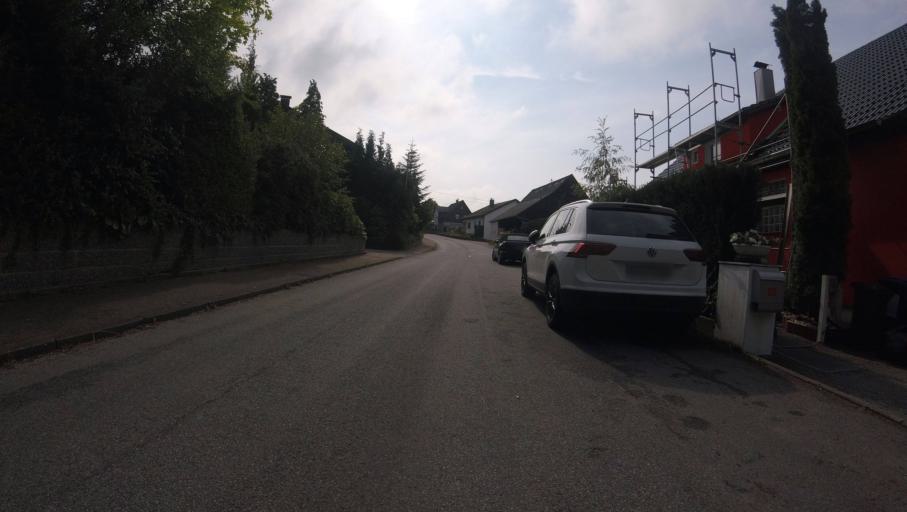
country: DE
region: Baden-Wuerttemberg
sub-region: Regierungsbezirk Stuttgart
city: Althutte
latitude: 48.9322
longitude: 9.5586
